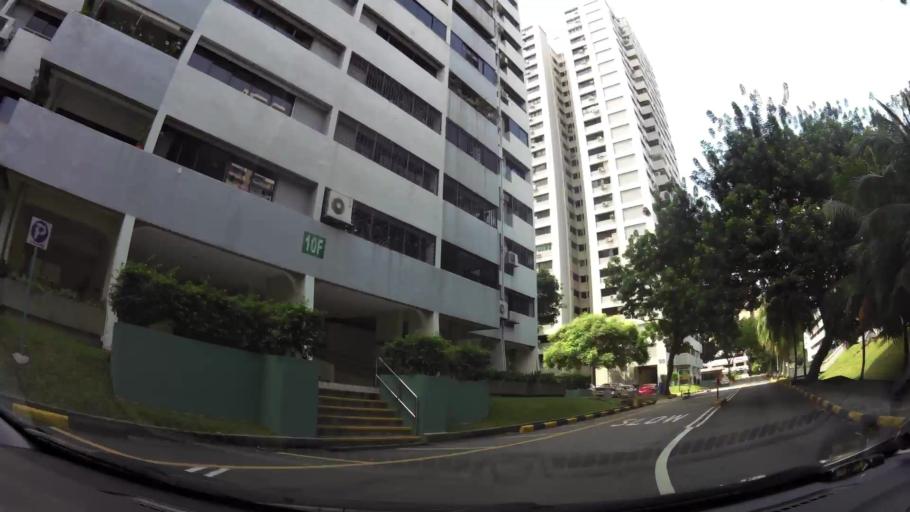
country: SG
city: Singapore
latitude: 1.3419
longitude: 103.8421
